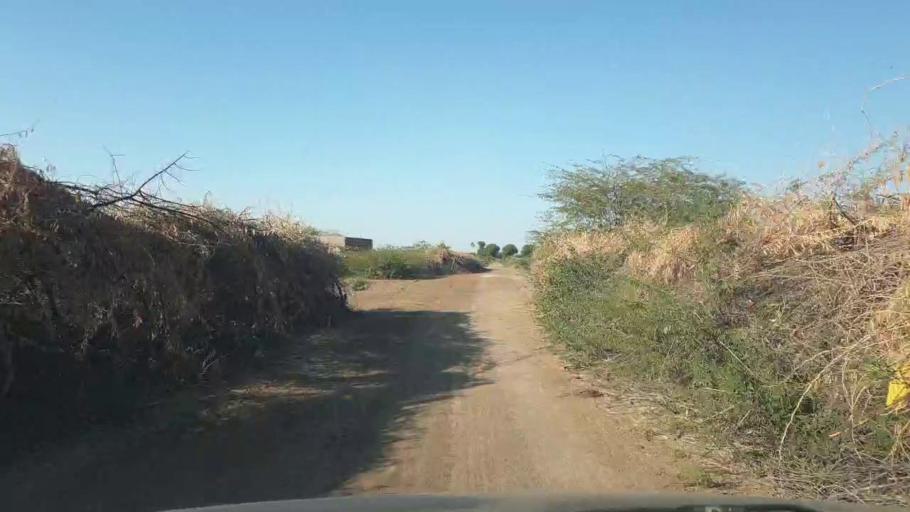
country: PK
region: Sindh
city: Dhoro Naro
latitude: 25.4307
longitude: 69.5438
